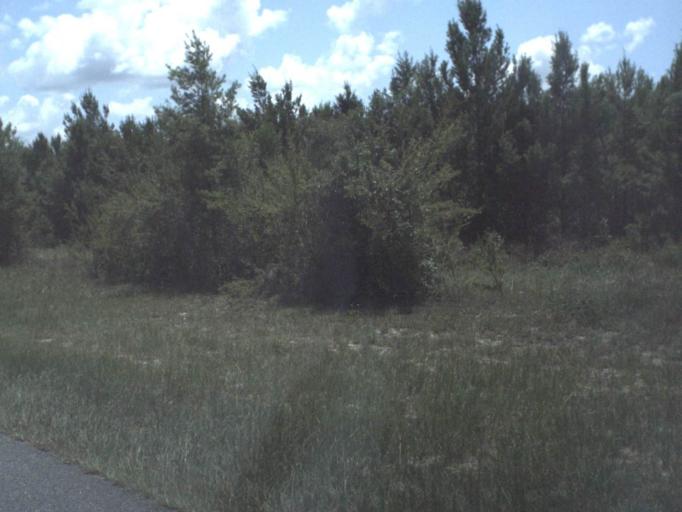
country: US
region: Florida
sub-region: Gilchrist County
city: Trenton
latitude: 29.7405
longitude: -82.7406
